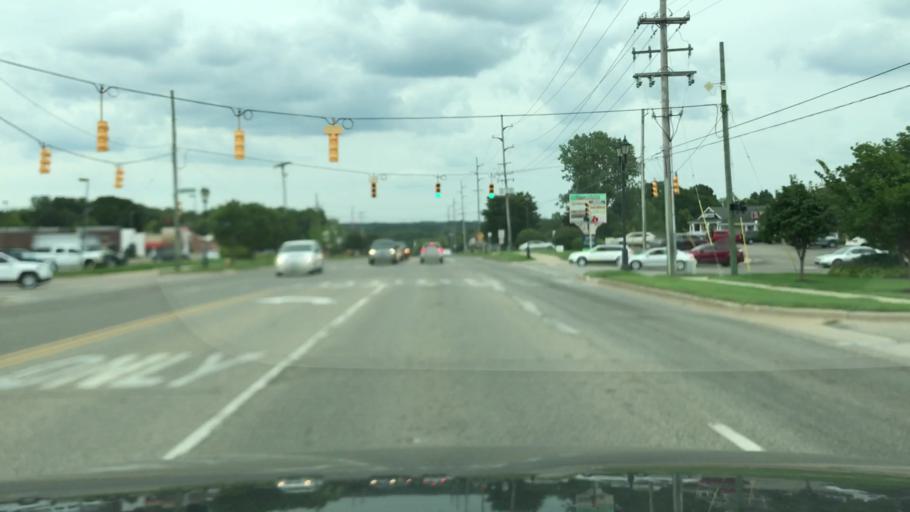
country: US
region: Michigan
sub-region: Kent County
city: Forest Hills
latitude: 42.9131
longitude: -85.5087
